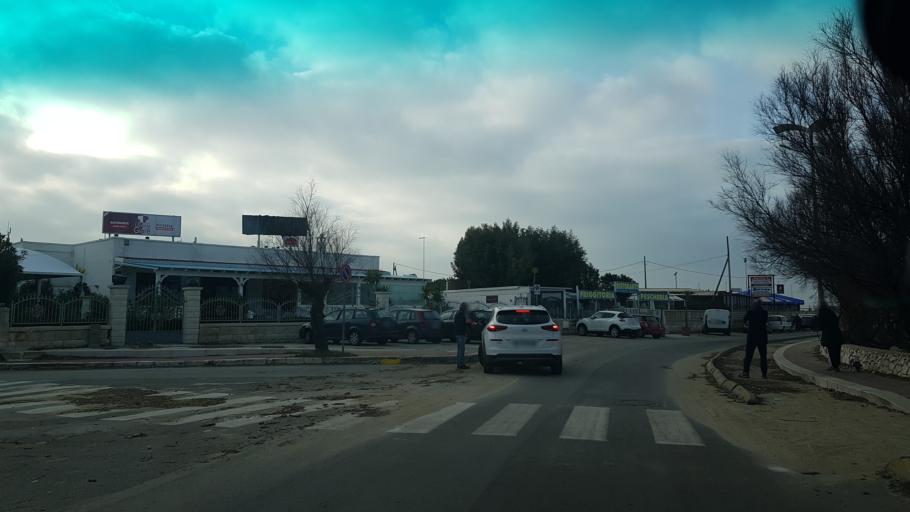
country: IT
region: Apulia
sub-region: Provincia di Brindisi
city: Carovigno
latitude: 40.7411
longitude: 17.7366
